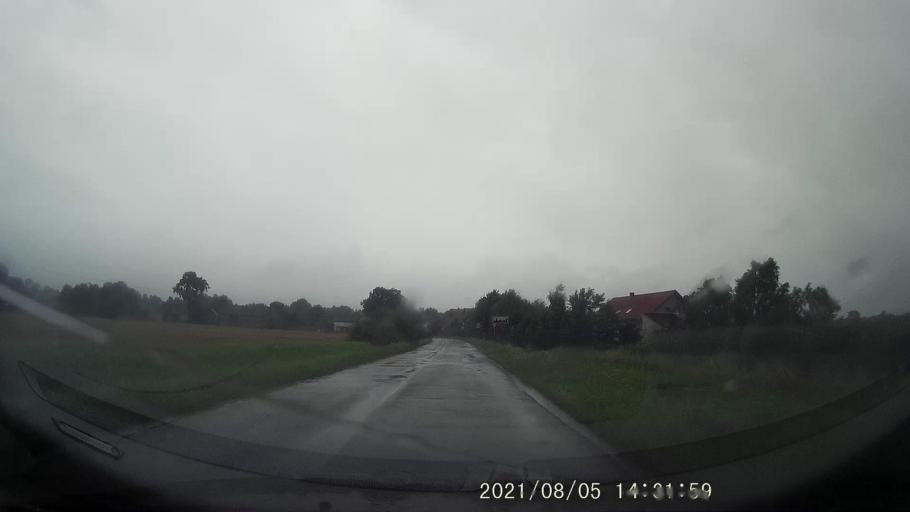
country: PL
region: Opole Voivodeship
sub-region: Powiat nyski
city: Korfantow
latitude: 50.4705
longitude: 17.5527
